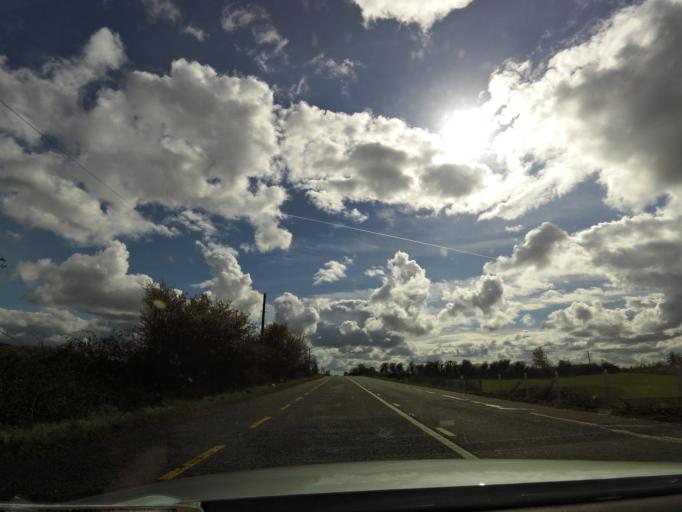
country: IE
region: Leinster
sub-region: Laois
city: Rathdowney
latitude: 52.7935
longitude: -7.5139
